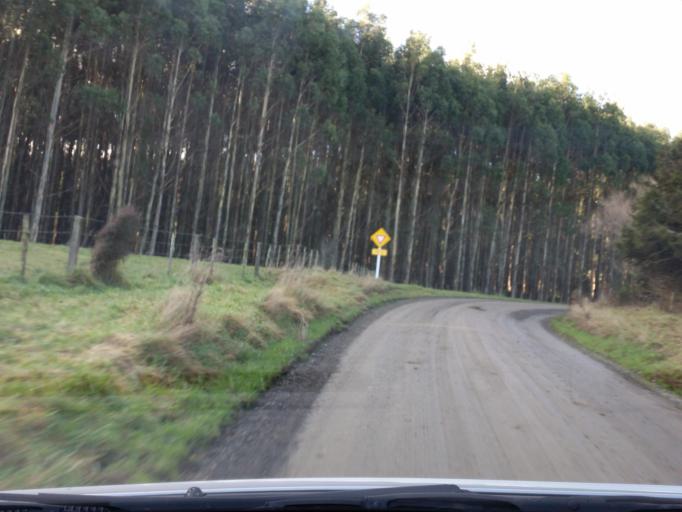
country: NZ
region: Otago
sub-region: Clutha District
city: Papatowai
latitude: -46.5858
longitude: 169.1534
